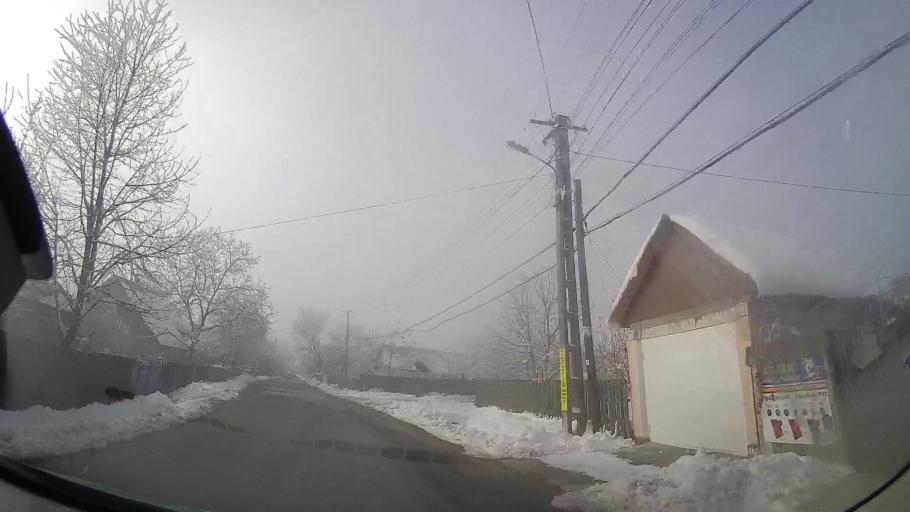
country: RO
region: Iasi
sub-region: Comuna Valea Seaca
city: Topile
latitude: 47.2532
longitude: 26.6647
